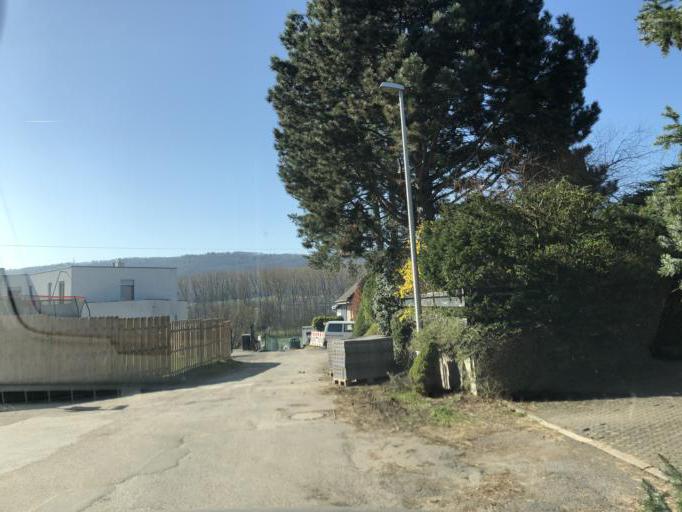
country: DE
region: North Rhine-Westphalia
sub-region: Regierungsbezirk Detmold
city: Minden
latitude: 52.2669
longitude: 8.8927
